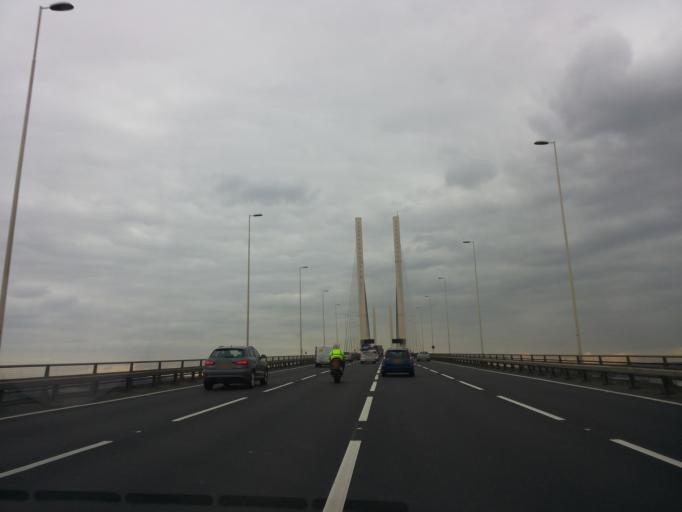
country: GB
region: England
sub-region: Kent
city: West Thurrock
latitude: 51.4693
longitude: 0.2629
